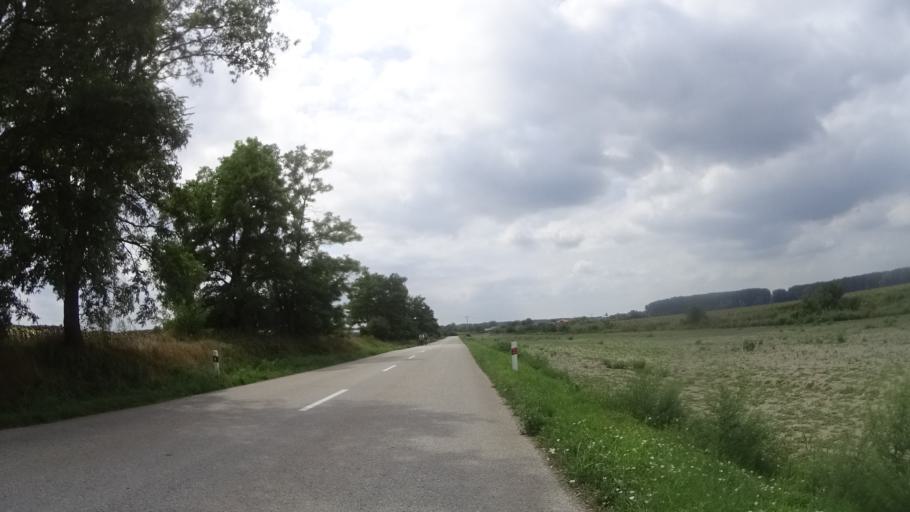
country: HU
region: Gyor-Moson-Sopron
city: Bony
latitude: 47.7570
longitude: 17.8320
